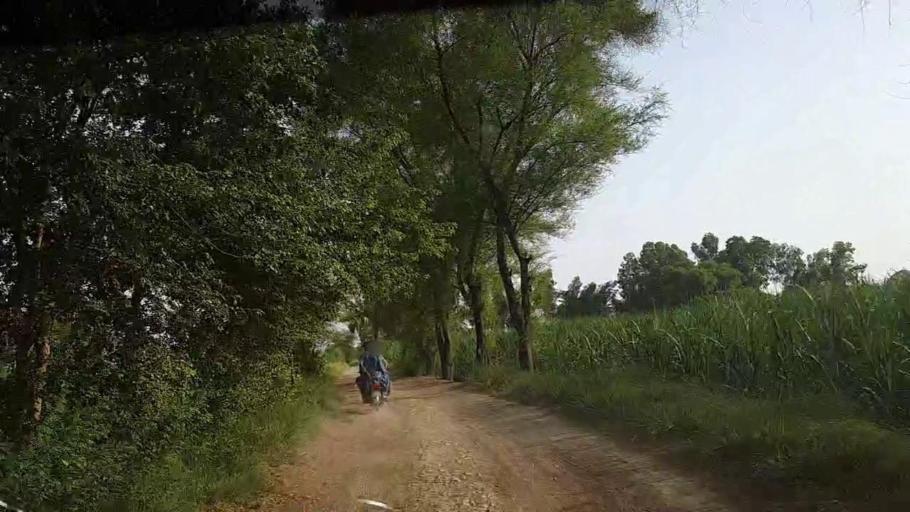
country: PK
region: Sindh
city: Ghotki
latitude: 27.9753
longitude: 69.2559
